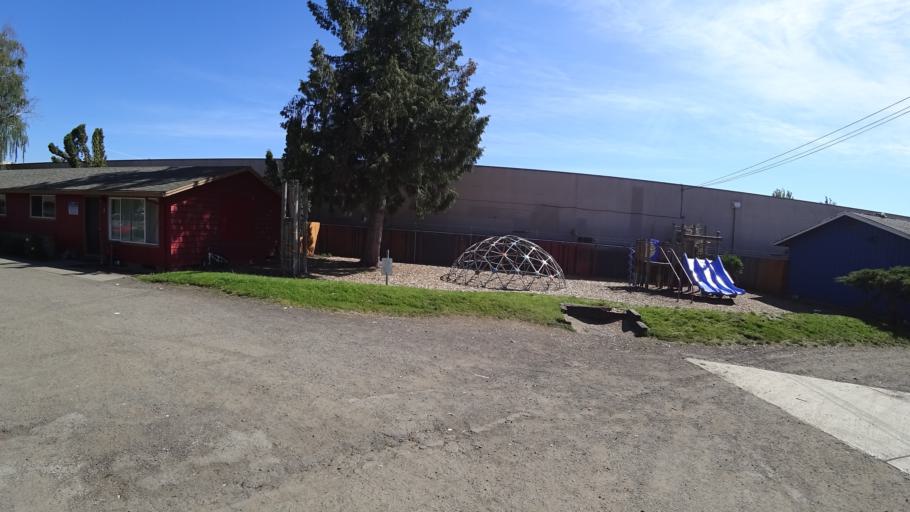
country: US
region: Oregon
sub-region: Washington County
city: Hillsboro
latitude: 45.5130
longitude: -122.9723
